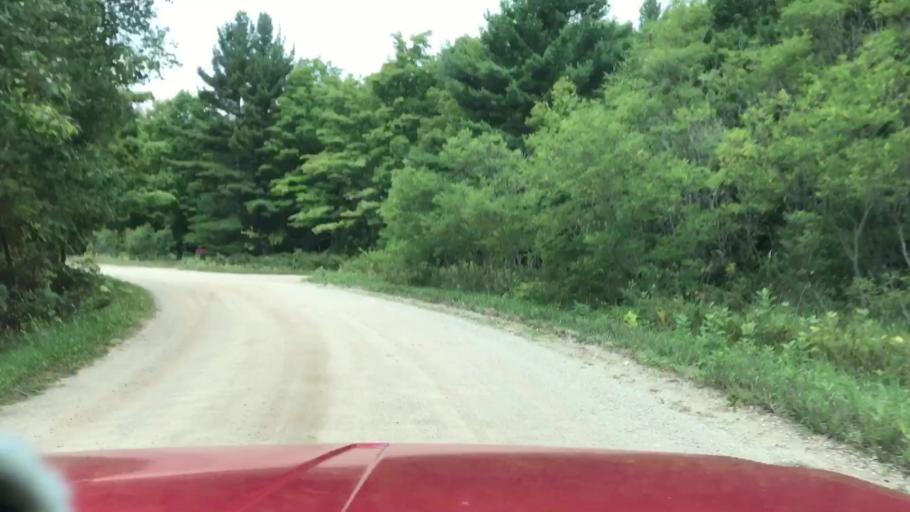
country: US
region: Michigan
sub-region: Charlevoix County
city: Charlevoix
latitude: 45.7216
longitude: -85.5628
